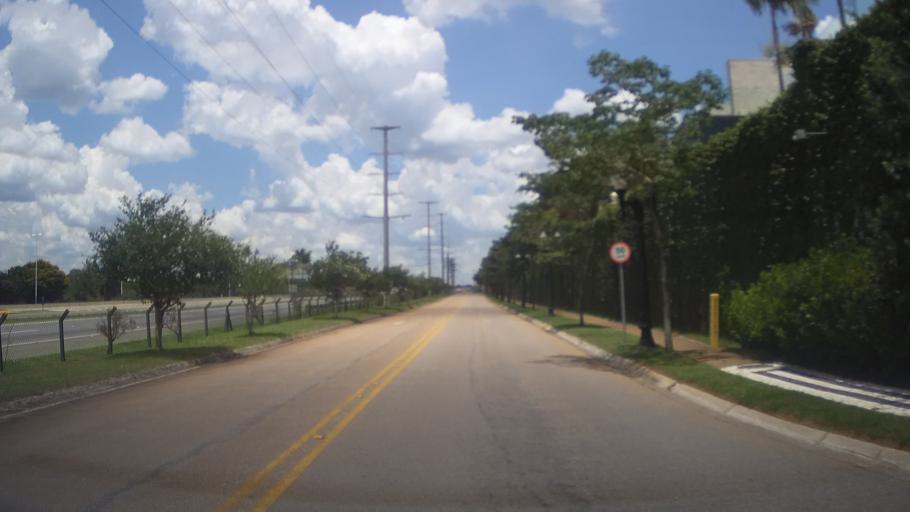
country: BR
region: Sao Paulo
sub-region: Jundiai
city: Jundiai
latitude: -23.1553
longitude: -46.8855
